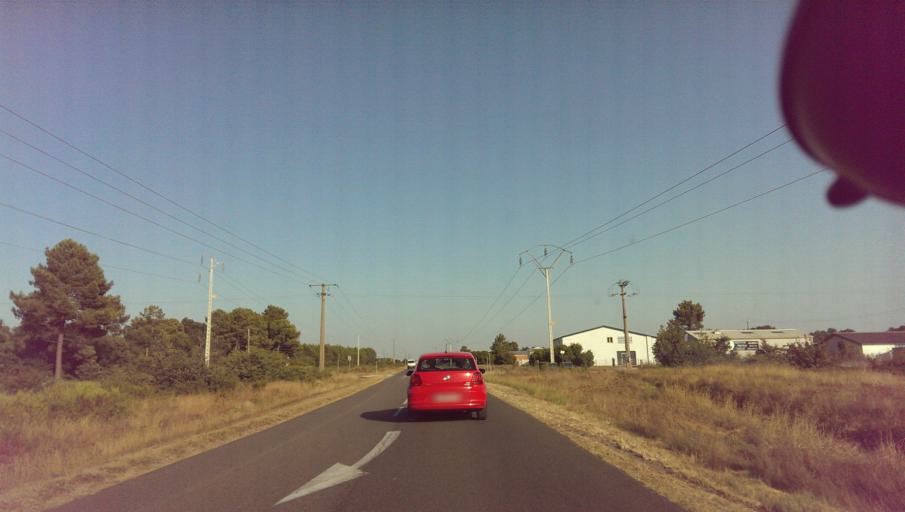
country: FR
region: Aquitaine
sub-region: Departement des Landes
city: Mimizan
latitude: 44.1912
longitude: -1.2163
